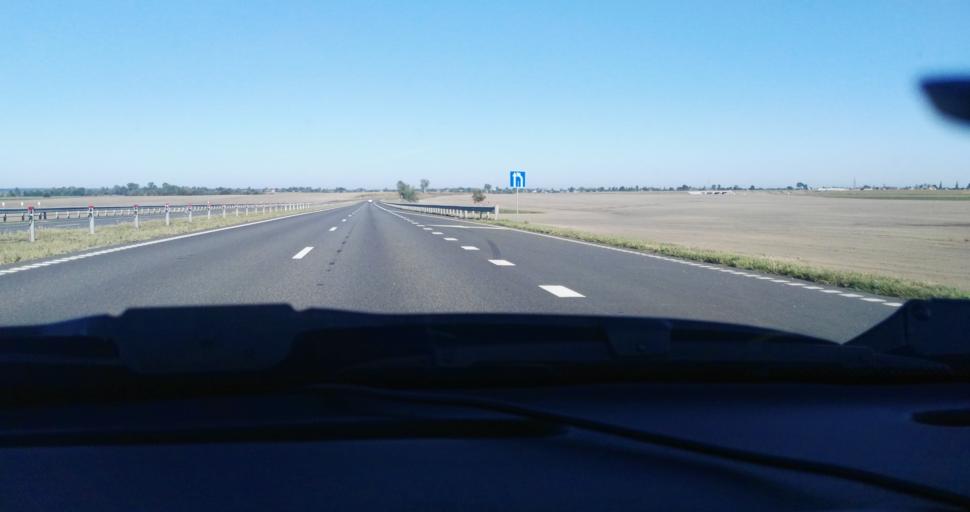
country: BY
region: Gomel
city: Buda-Kashalyova
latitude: 52.5056
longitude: 30.6431
